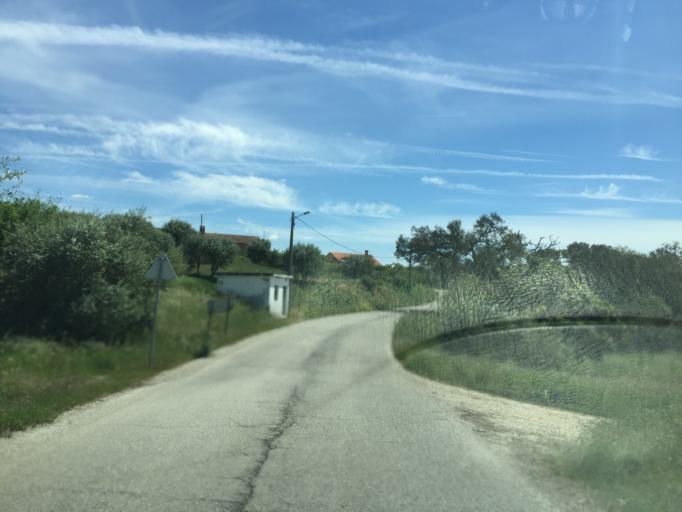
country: PT
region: Coimbra
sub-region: Soure
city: Soure
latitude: 40.0526
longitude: -8.6742
